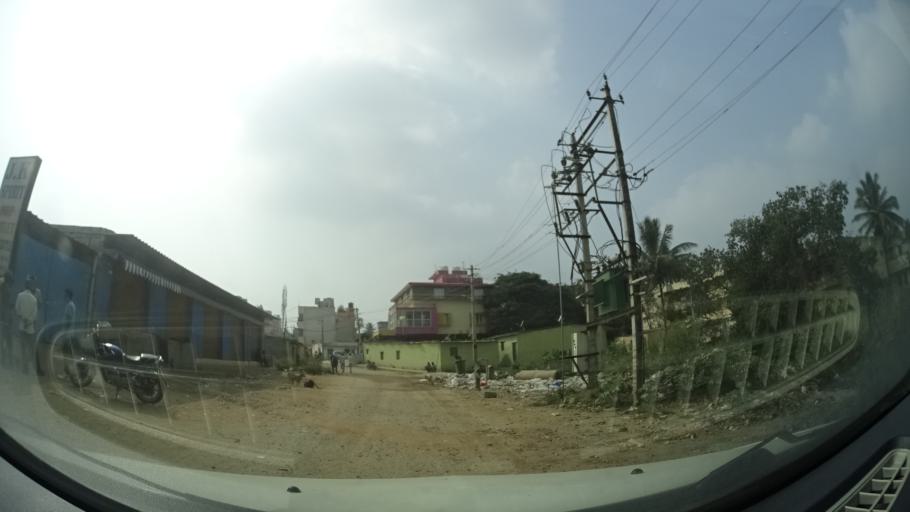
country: IN
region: Karnataka
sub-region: Bangalore Urban
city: Anekal
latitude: 12.8253
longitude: 77.6687
